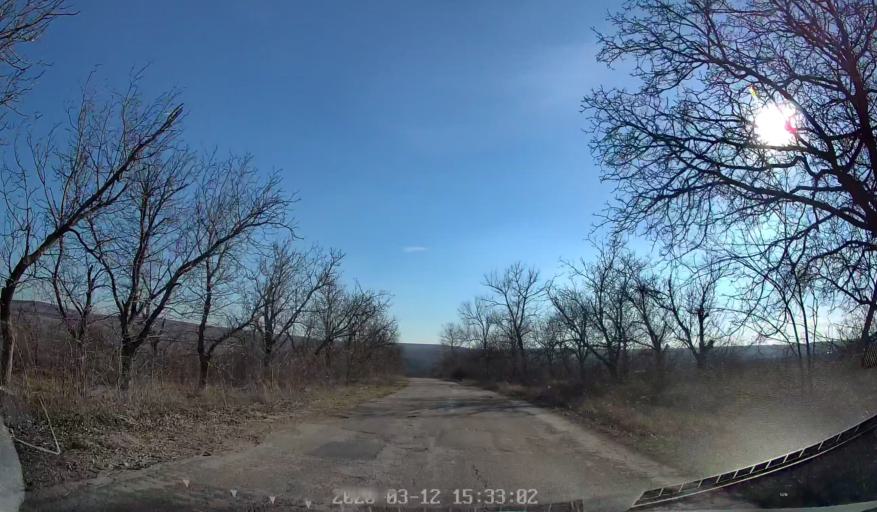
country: MD
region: Chisinau
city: Ciorescu
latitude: 47.1467
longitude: 28.9385
